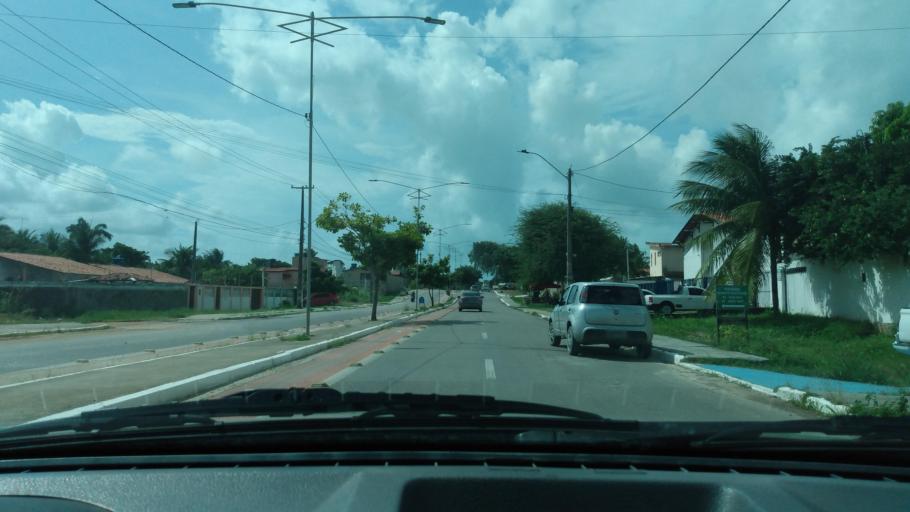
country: BR
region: Pernambuco
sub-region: Cabo De Santo Agostinho
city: Cabo
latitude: -8.3135
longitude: -34.9491
